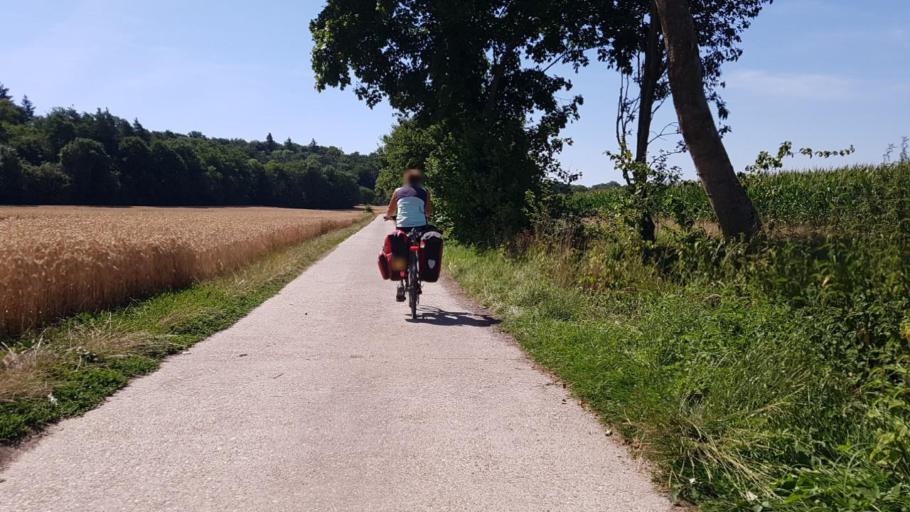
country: DE
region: Baden-Wuerttemberg
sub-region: Karlsruhe Region
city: Sulzfeld
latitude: 49.1466
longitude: 8.8658
